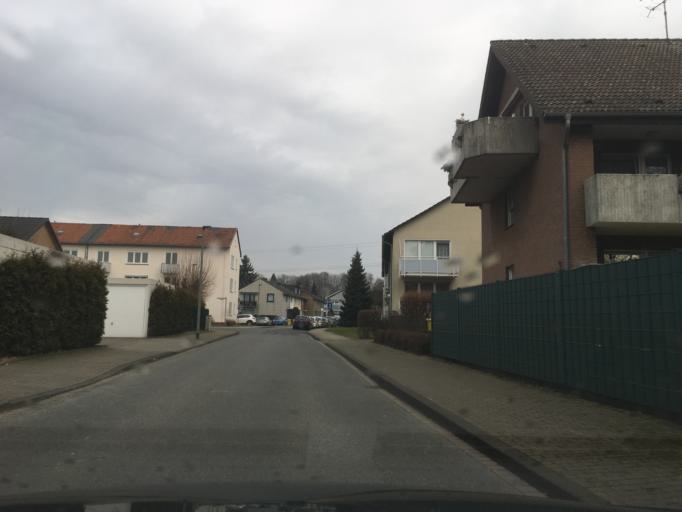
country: DE
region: North Rhine-Westphalia
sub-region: Regierungsbezirk Munster
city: Gladbeck
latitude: 51.5517
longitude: 7.0262
